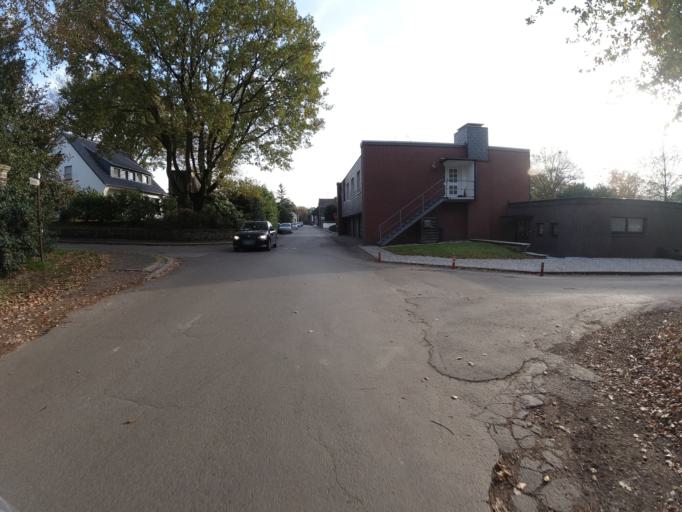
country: DE
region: North Rhine-Westphalia
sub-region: Regierungsbezirk Dusseldorf
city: Moers
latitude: 51.4252
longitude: 6.6450
